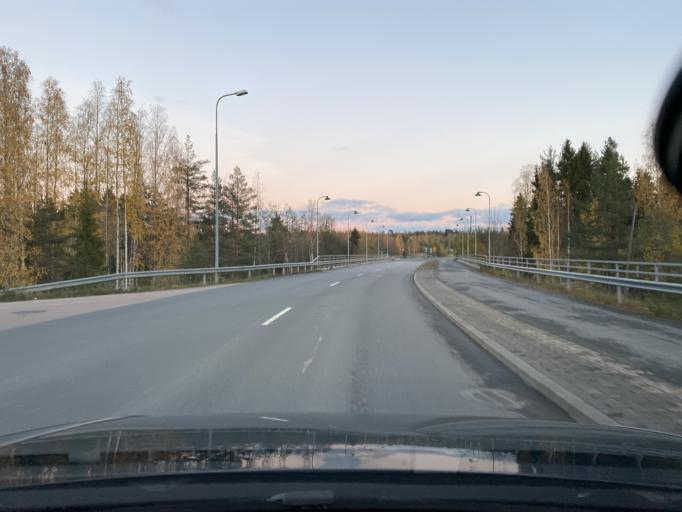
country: FI
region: Pirkanmaa
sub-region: Tampere
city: Lempaeaelae
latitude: 61.3284
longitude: 23.7642
